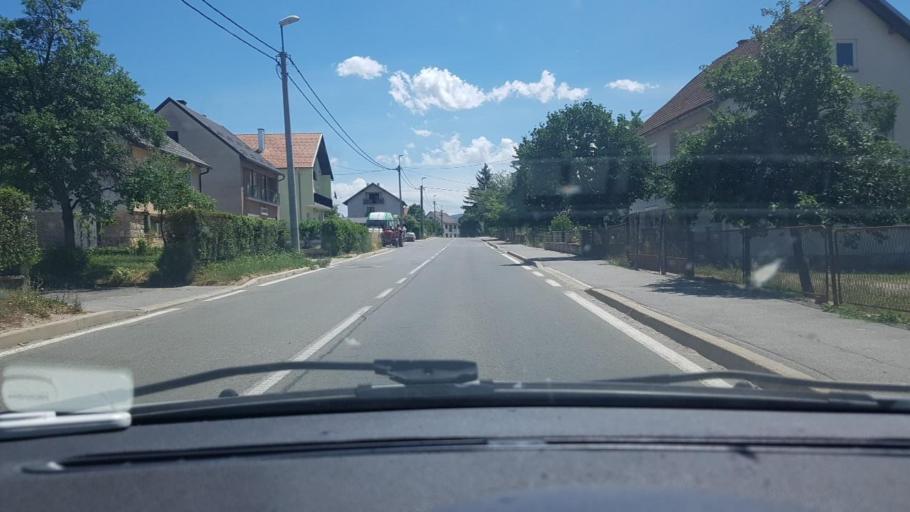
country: HR
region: Licko-Senjska
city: Otocac
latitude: 44.8666
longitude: 15.2546
